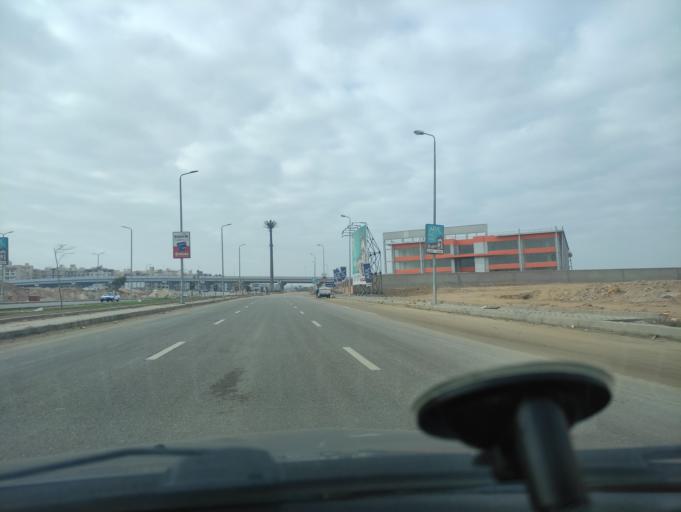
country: EG
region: Muhafazat al Qalyubiyah
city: Al Khankah
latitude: 30.0452
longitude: 31.5256
